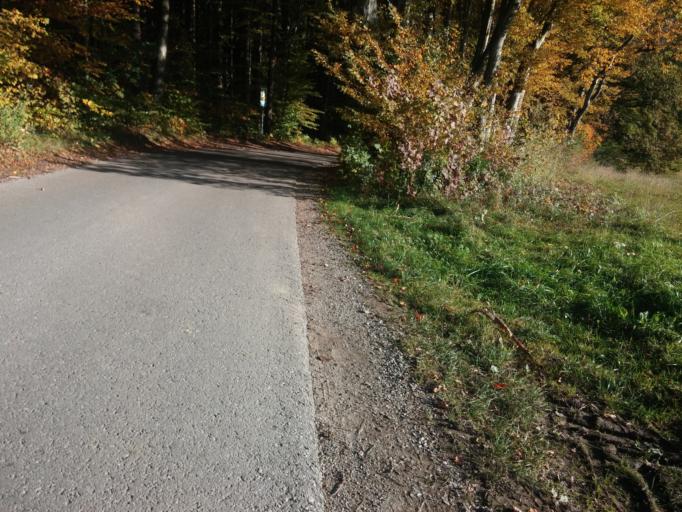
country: DE
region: Bavaria
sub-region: Upper Bavaria
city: Aying
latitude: 47.9654
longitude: 11.7887
